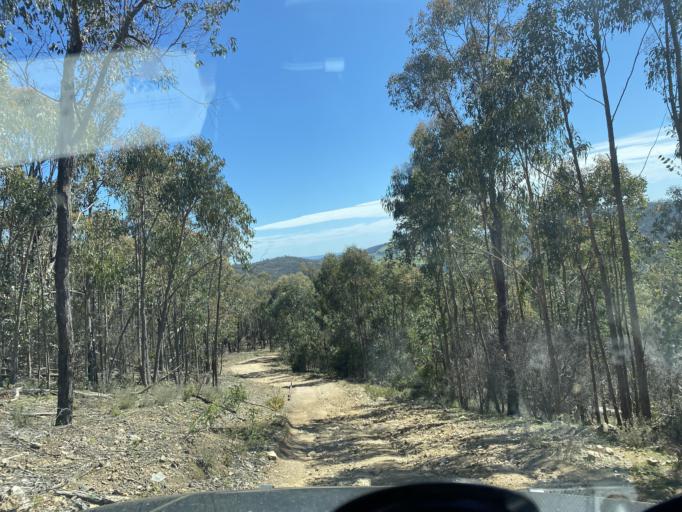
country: AU
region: Victoria
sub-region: Benalla
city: Benalla
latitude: -36.7219
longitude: 146.1821
